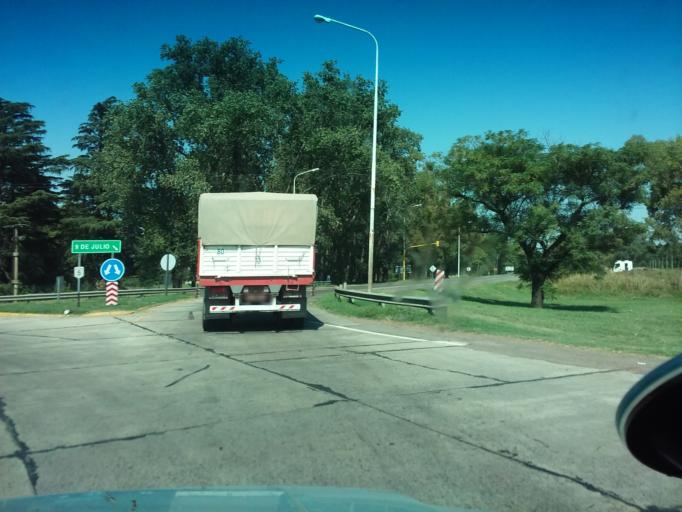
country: AR
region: Buenos Aires
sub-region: Partido de Alberti
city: Alberti
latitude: -35.0540
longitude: -60.2645
